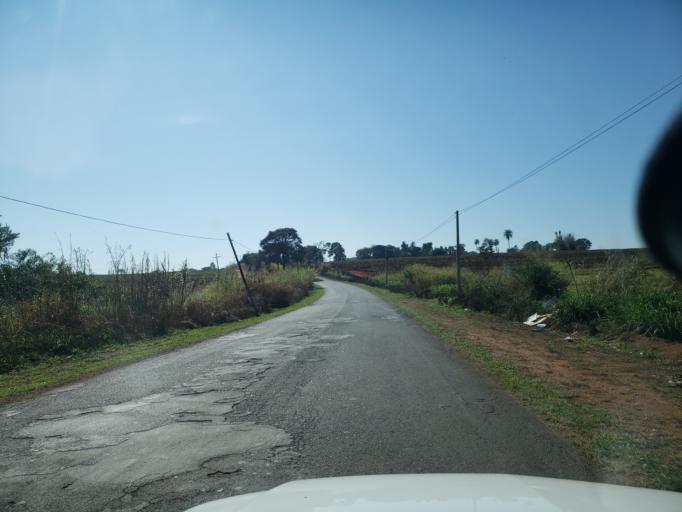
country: BR
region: Sao Paulo
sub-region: Moji-Guacu
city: Mogi-Gaucu
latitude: -22.3517
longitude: -46.8976
